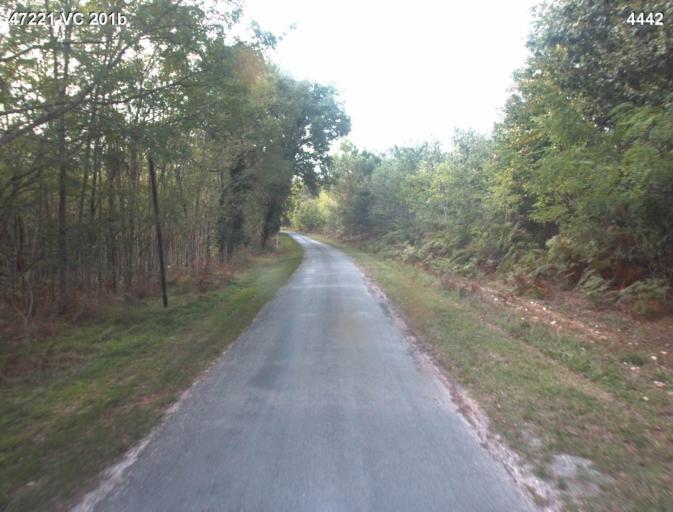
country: FR
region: Aquitaine
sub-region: Departement du Lot-et-Garonne
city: Mezin
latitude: 44.0905
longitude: 0.2002
